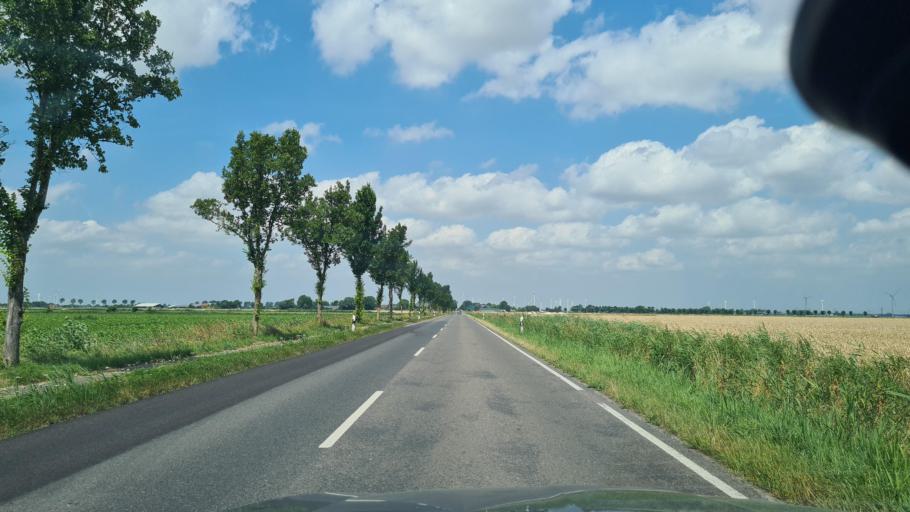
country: DE
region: Schleswig-Holstein
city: Wohrden
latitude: 54.1338
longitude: 9.0167
